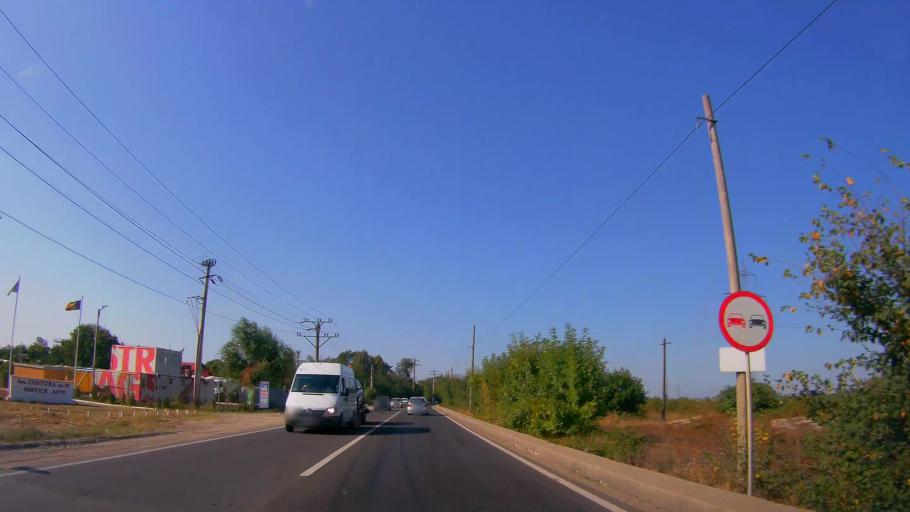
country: RO
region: Ilfov
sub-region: Comuna Clinceni
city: Olteni
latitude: 44.4150
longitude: 25.9712
